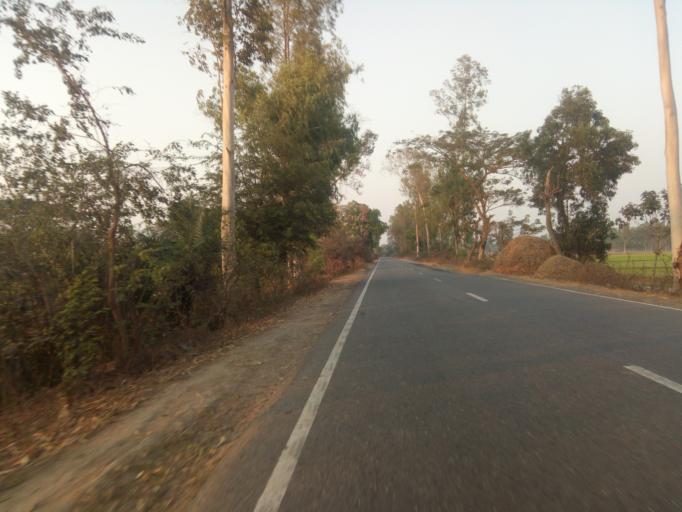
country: BD
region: Rajshahi
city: Bogra
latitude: 24.6201
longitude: 89.2413
